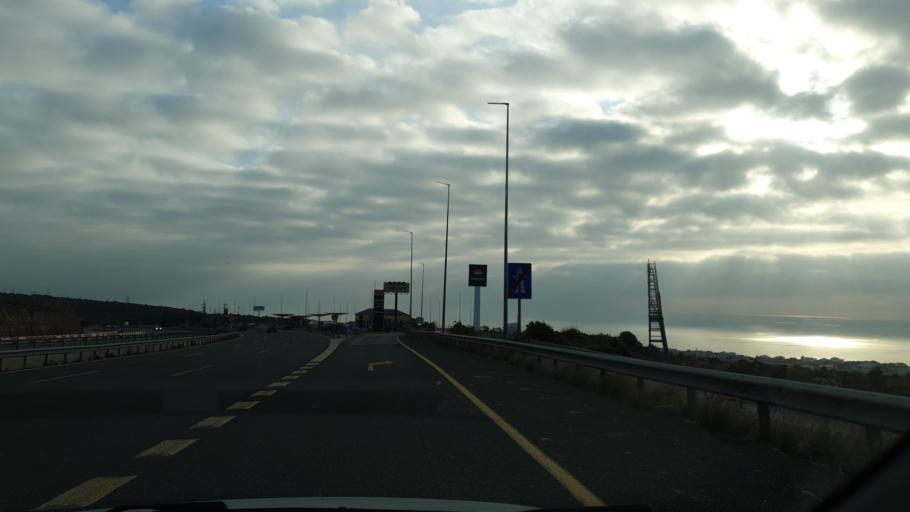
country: ES
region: Andalusia
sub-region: Provincia de Malaga
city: Torremolinos
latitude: 36.6105
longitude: -4.5314
